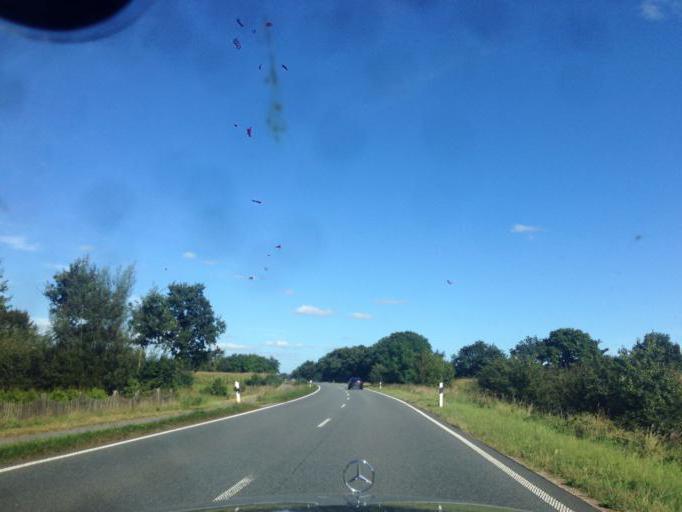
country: DE
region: Schleswig-Holstein
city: Nordhackstedt
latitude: 54.7544
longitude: 9.1416
